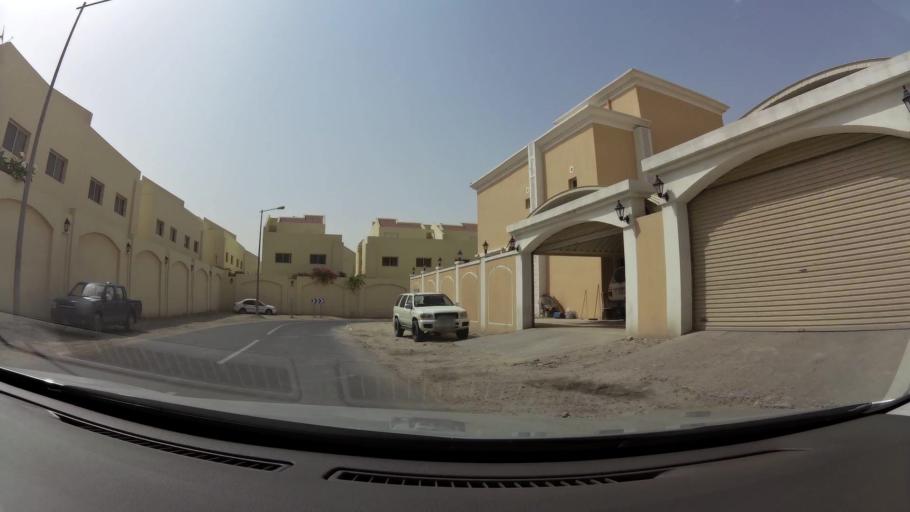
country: QA
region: Baladiyat ad Dawhah
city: Doha
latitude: 25.3061
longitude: 51.4823
